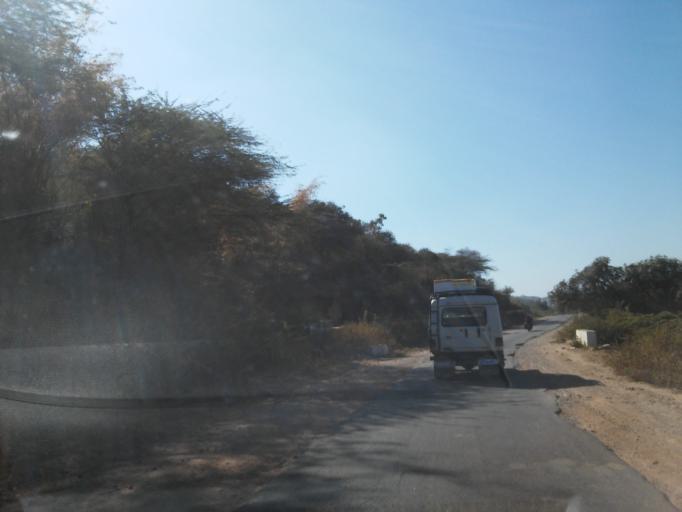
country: IN
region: Rajasthan
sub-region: Udaipur
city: Udaipur
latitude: 24.5312
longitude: 73.6240
